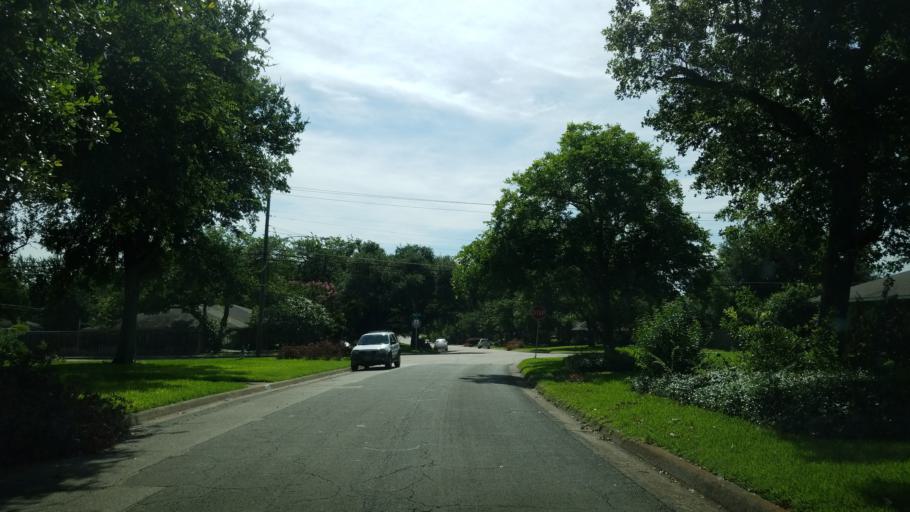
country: US
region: Texas
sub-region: Dallas County
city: Farmers Branch
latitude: 32.9043
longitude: -96.8520
